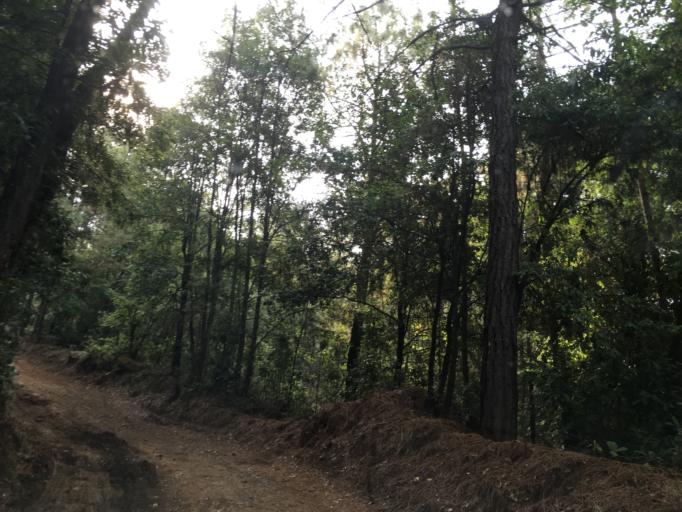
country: MX
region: Michoacan
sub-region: Zitacuaro
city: La Fundicion (Quinta Manzana)
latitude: 19.4974
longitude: -100.3093
